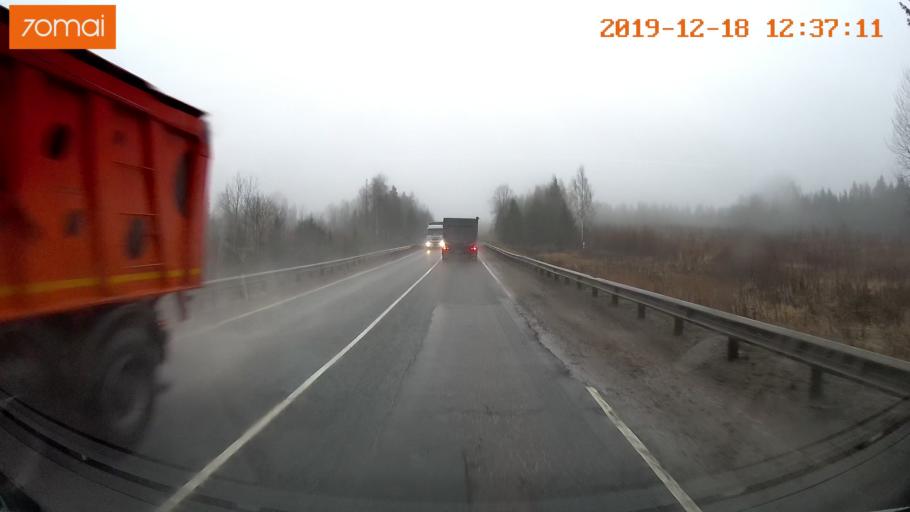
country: RU
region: Moskovskaya
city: Vysokovsk
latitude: 56.1432
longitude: 36.5998
